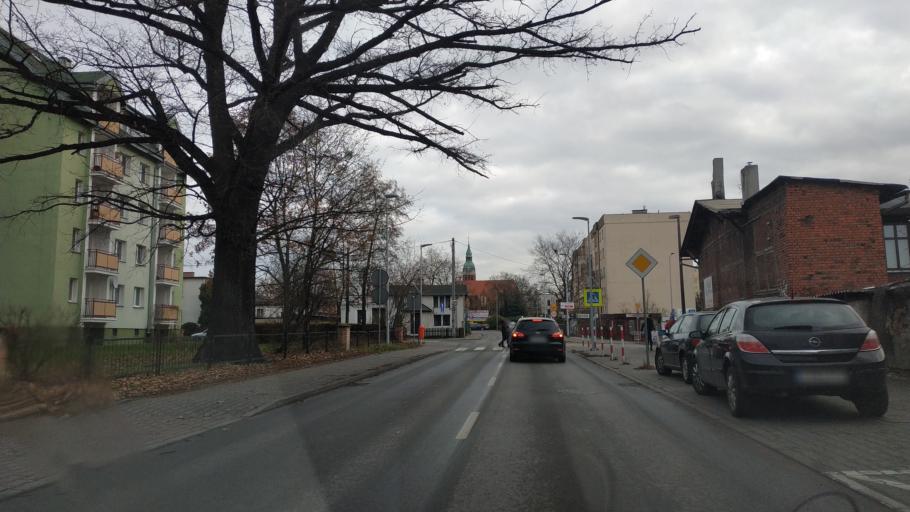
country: PL
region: Kujawsko-Pomorskie
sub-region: Torun
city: Torun
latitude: 53.0223
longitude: 18.6058
